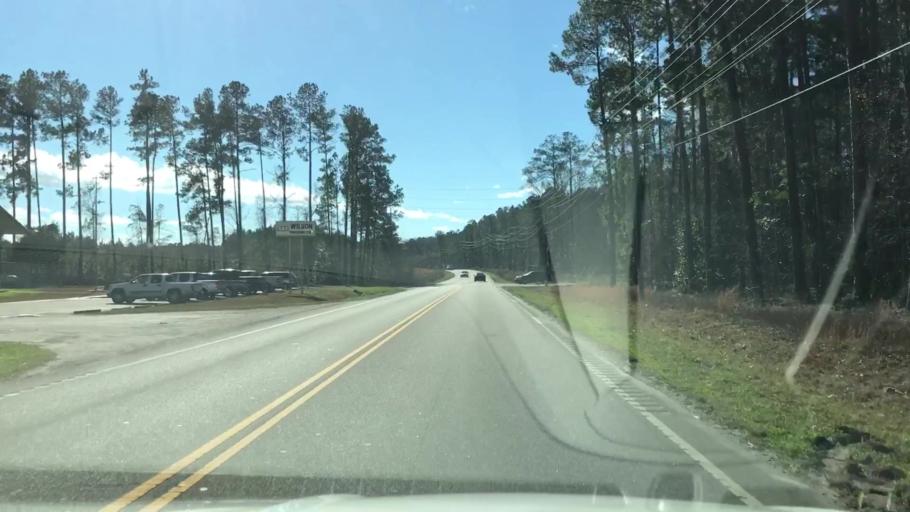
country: US
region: South Carolina
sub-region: Dorchester County
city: Summerville
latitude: 33.0767
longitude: -80.2146
